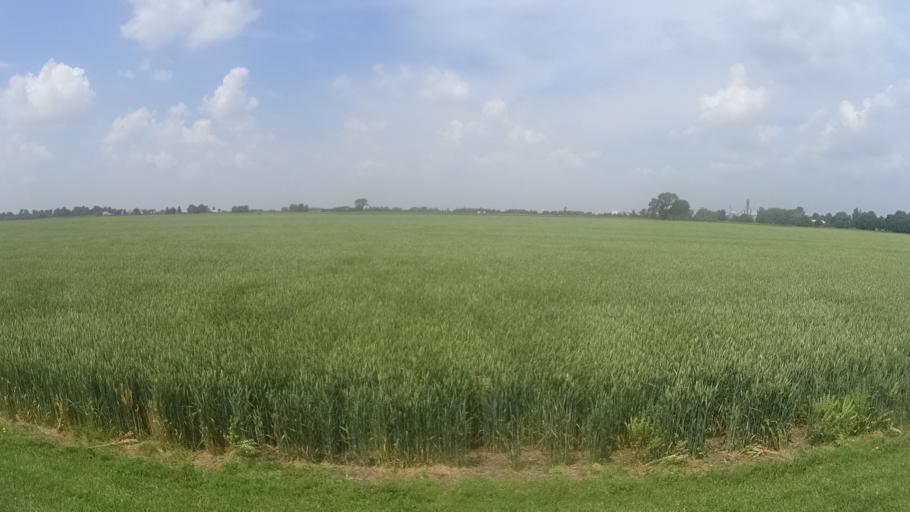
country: US
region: Ohio
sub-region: Huron County
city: Monroeville
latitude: 41.3294
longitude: -82.6935
